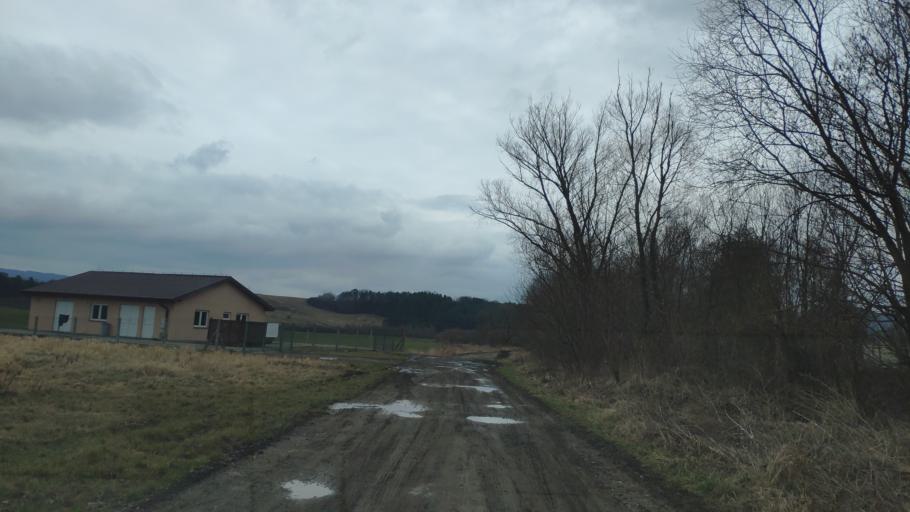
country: SK
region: Presovsky
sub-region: Okres Presov
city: Presov
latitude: 49.0897
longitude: 21.2764
